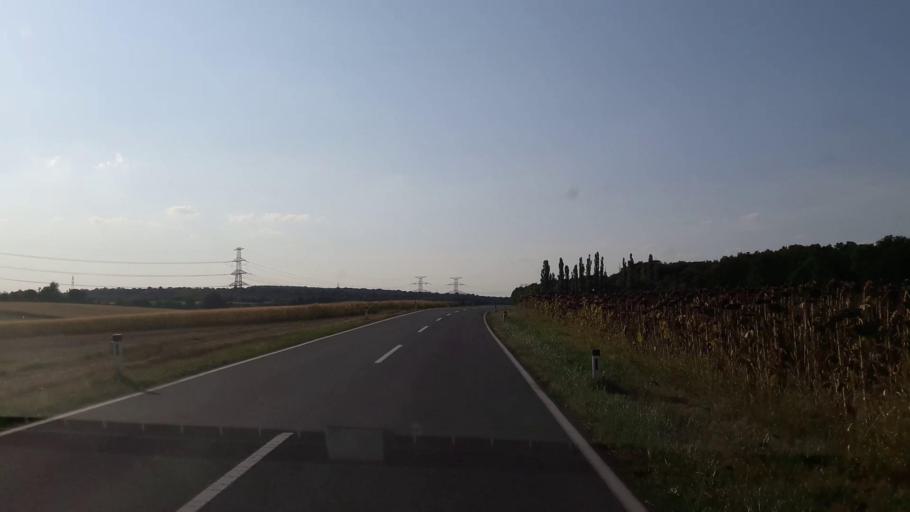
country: AT
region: Lower Austria
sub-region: Politischer Bezirk Ganserndorf
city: Orth an der Donau
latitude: 48.0736
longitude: 16.6922
